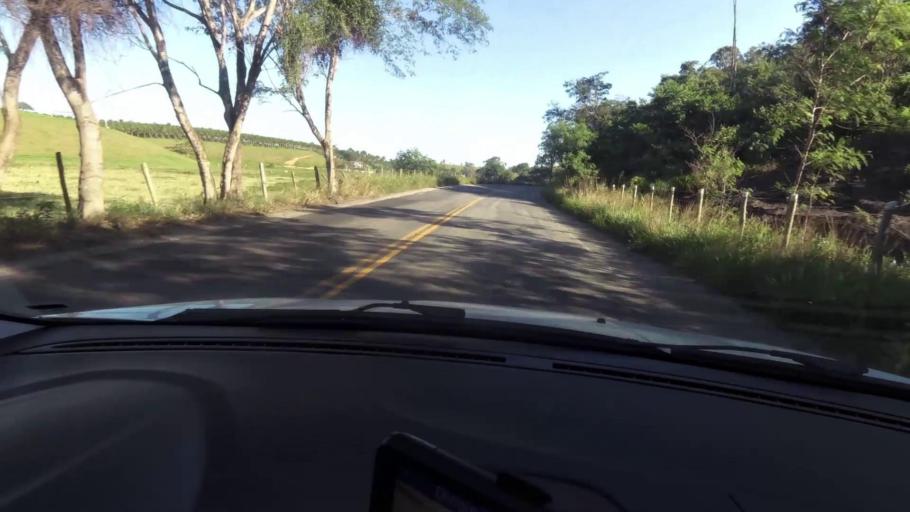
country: BR
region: Espirito Santo
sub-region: Piuma
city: Piuma
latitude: -20.7435
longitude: -40.6482
